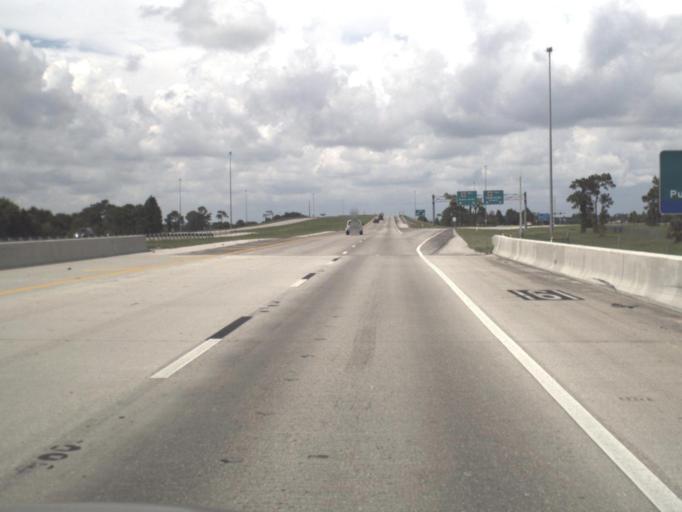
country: US
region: Florida
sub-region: Charlotte County
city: Charlotte Park
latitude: 26.8913
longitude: -81.9979
